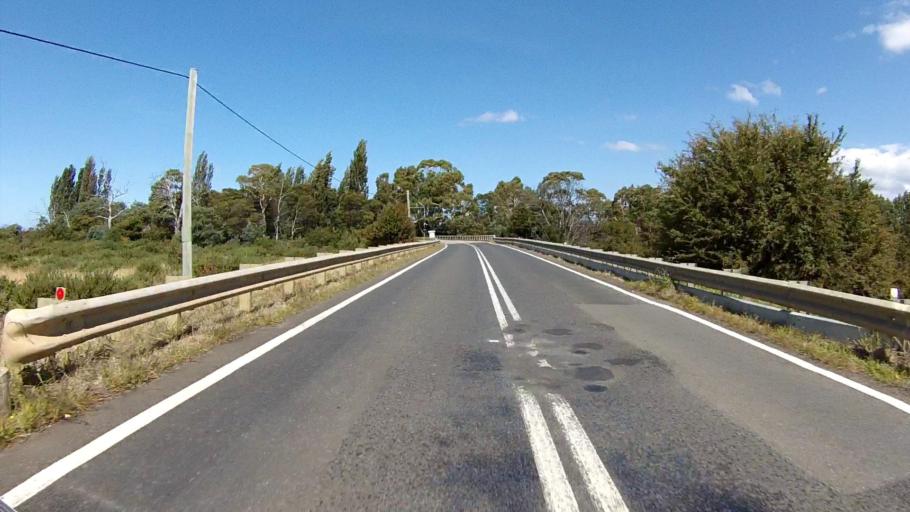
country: AU
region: Tasmania
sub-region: Break O'Day
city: St Helens
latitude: -42.0672
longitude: 148.0638
